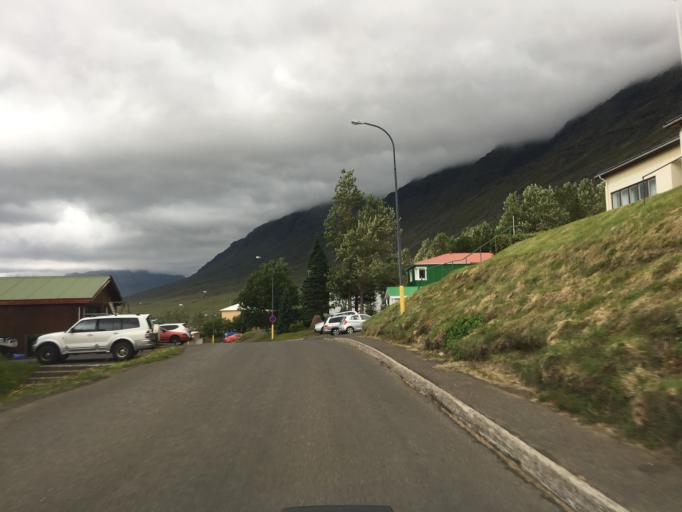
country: IS
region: East
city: Neskaupstadur
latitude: 65.1490
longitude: -13.7014
